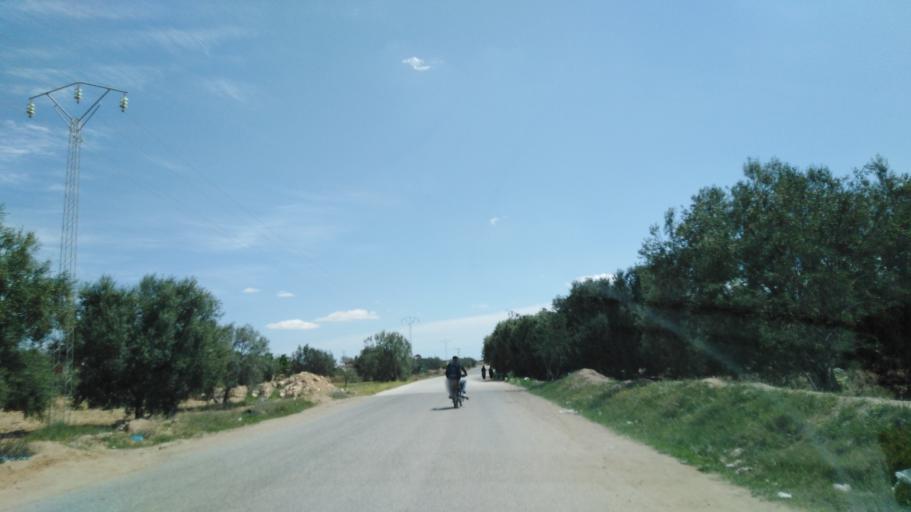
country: TN
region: Safaqis
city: Sfax
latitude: 34.7400
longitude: 10.5357
